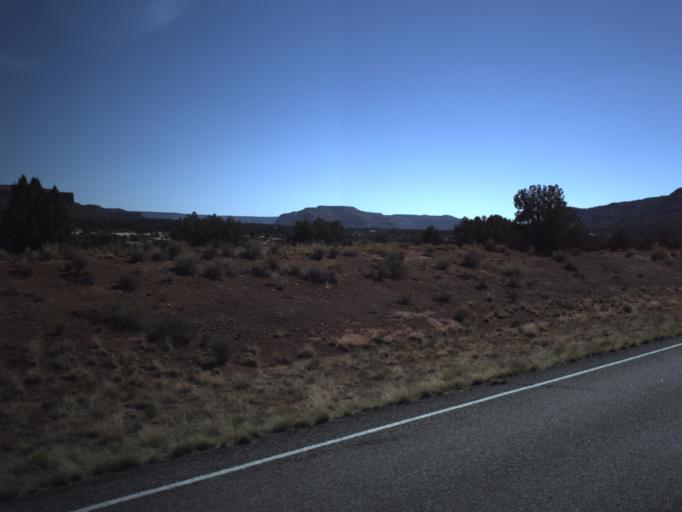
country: US
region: Utah
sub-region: San Juan County
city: Blanding
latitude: 37.6854
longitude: -110.2220
